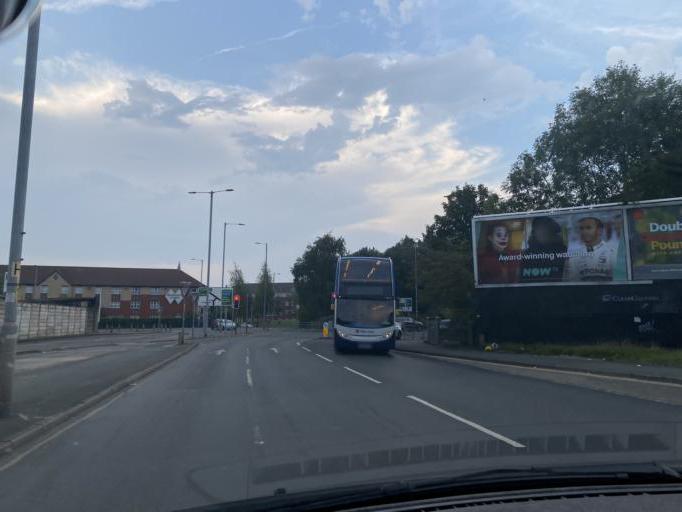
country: GB
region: England
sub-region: Manchester
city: Longsight
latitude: 53.4617
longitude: -2.1821
